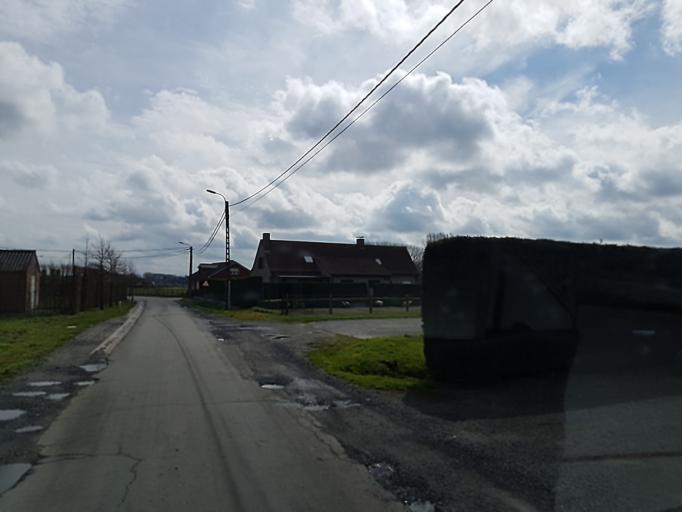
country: BE
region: Flanders
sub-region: Provincie Oost-Vlaanderen
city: Kruishoutem
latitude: 50.9343
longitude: 3.5036
